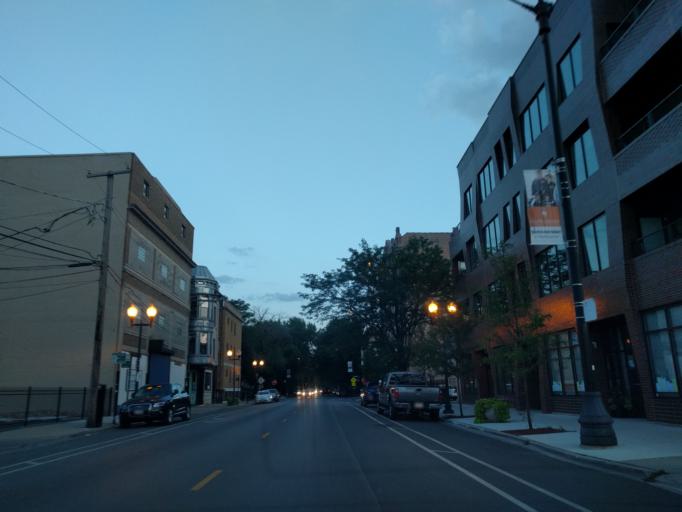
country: US
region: Illinois
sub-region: Cook County
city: Lincolnwood
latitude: 41.9531
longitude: -87.6788
